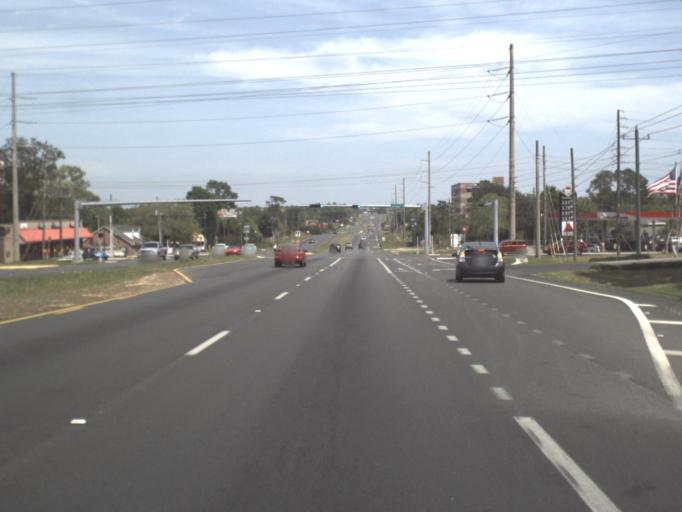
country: US
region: Florida
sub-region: Escambia County
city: Ferry Pass
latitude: 30.5325
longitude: -87.2384
